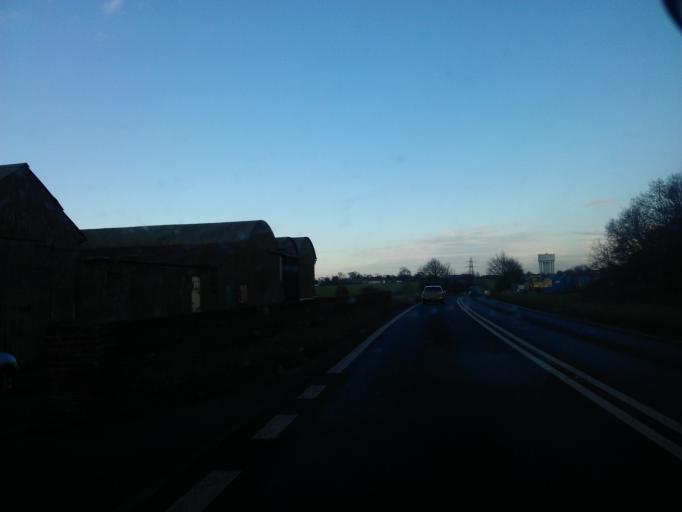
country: GB
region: England
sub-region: Essex
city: Mistley
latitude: 51.9001
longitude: 1.0731
